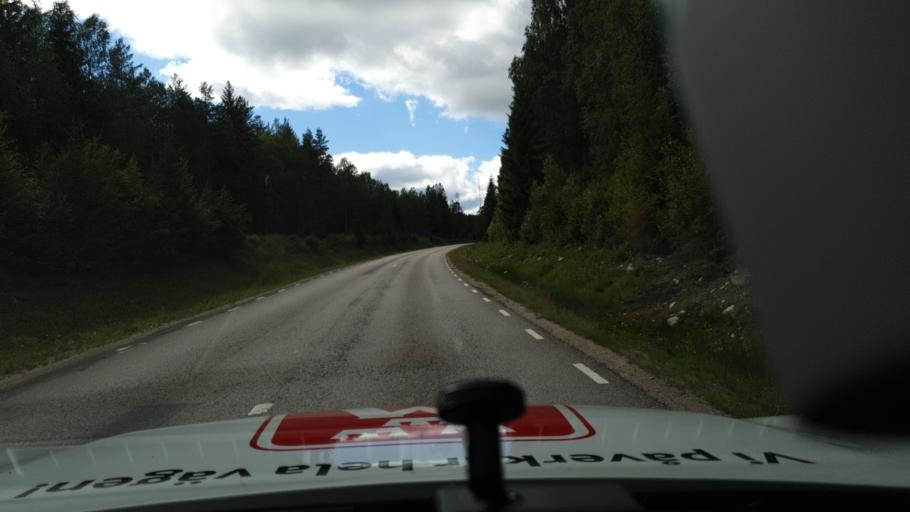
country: NO
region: Hedmark
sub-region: Trysil
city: Innbygda
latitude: 61.0180
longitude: 12.5274
